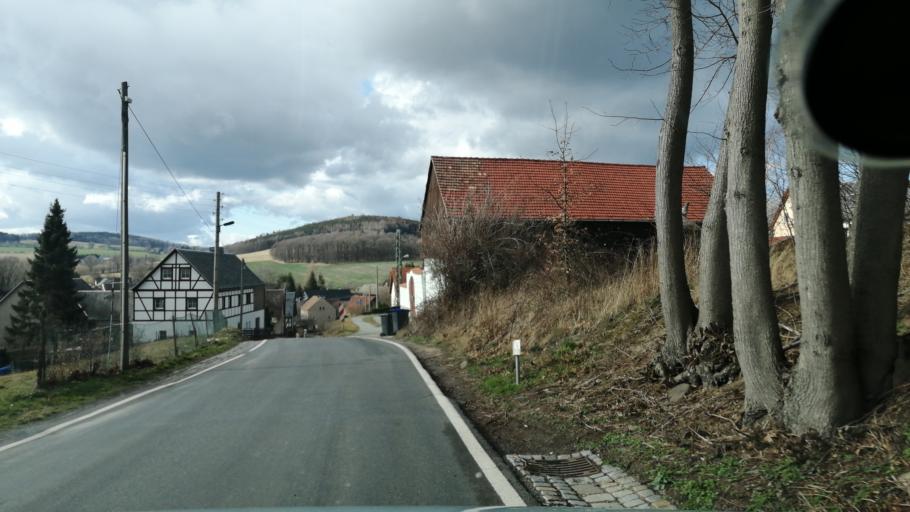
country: DE
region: Saxony
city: Kubschutz
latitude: 51.1372
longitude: 14.5176
